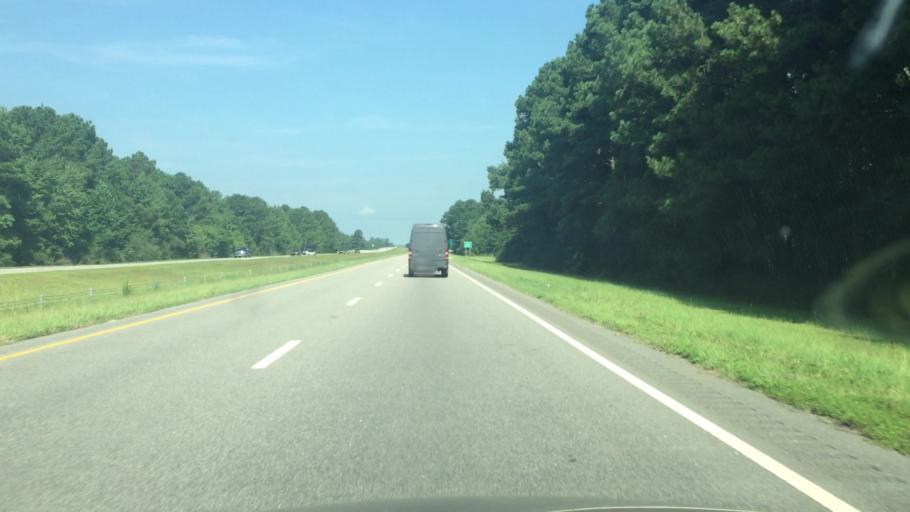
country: US
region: North Carolina
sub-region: Robeson County
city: Lumberton
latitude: 34.5752
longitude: -79.0395
